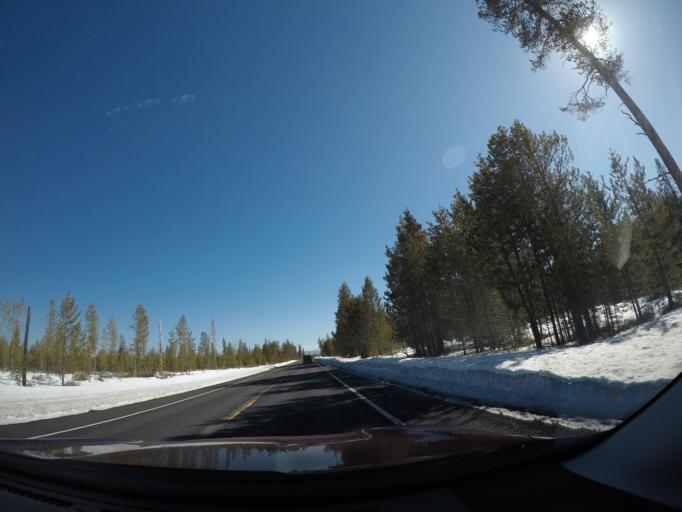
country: US
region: Oregon
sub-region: Deschutes County
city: Three Rivers
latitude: 43.8745
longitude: -121.5557
